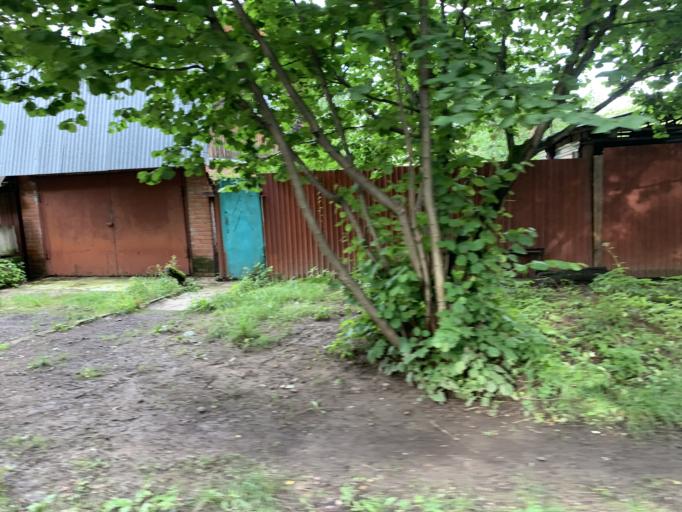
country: RU
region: Moskovskaya
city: Mamontovka
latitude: 55.9818
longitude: 37.8366
